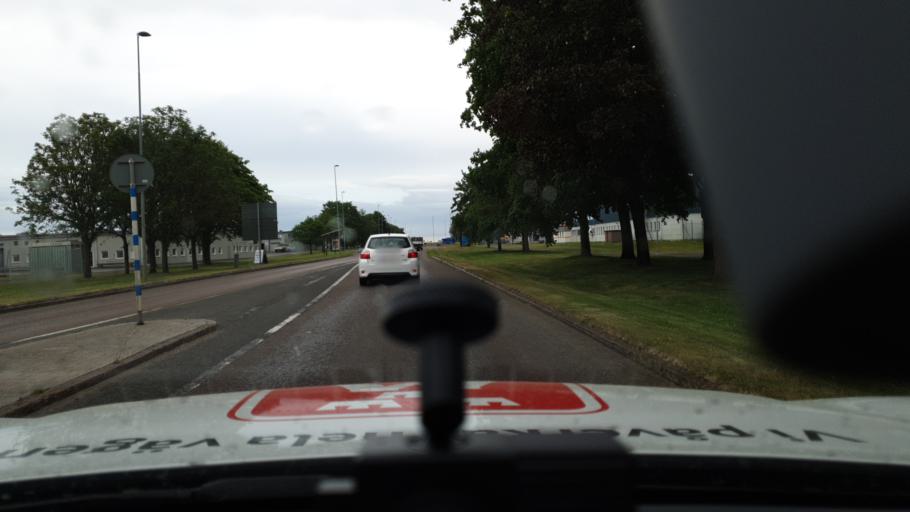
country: SE
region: Vaestra Goetaland
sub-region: Falkopings Kommun
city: Falkoeping
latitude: 58.1625
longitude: 13.5667
